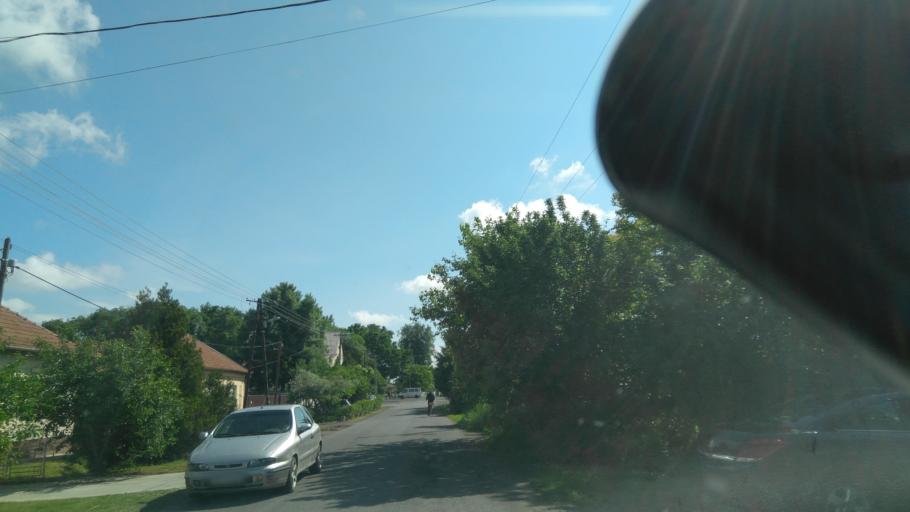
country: HU
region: Bekes
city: Bekes
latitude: 46.7756
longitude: 21.1172
